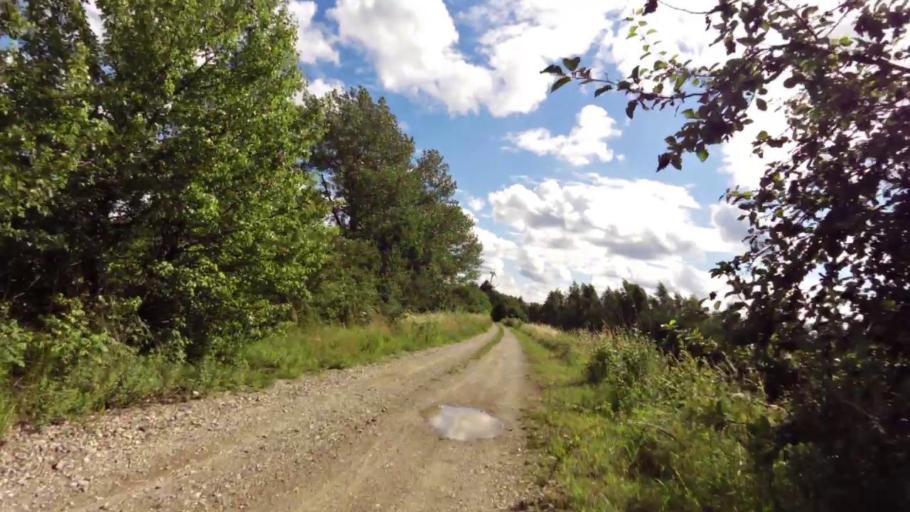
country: PL
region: West Pomeranian Voivodeship
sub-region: Powiat slawienski
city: Slawno
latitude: 54.5100
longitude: 16.7052
